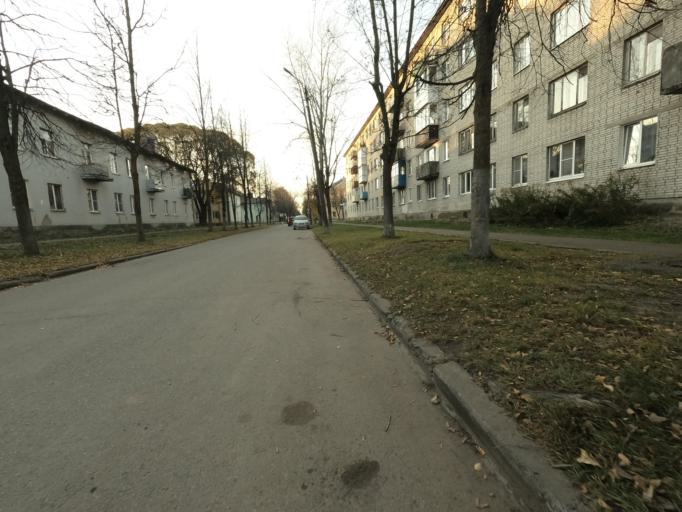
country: RU
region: Leningrad
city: Kirovsk
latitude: 59.8722
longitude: 30.9962
